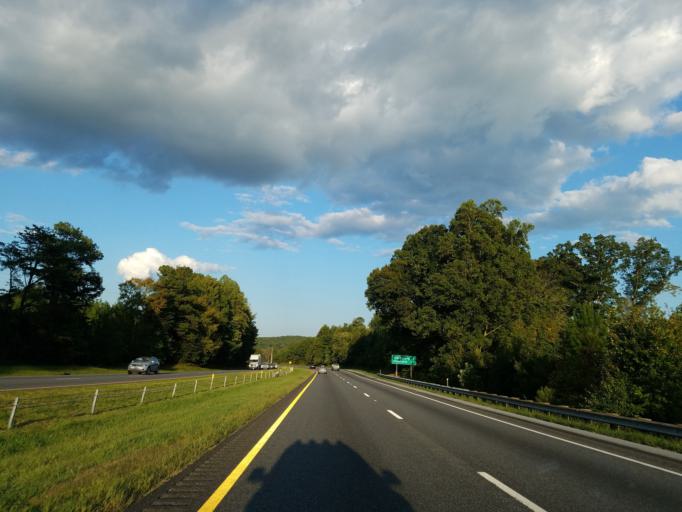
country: US
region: South Carolina
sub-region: Cherokee County
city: East Gaffney
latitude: 35.1104
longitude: -81.5901
